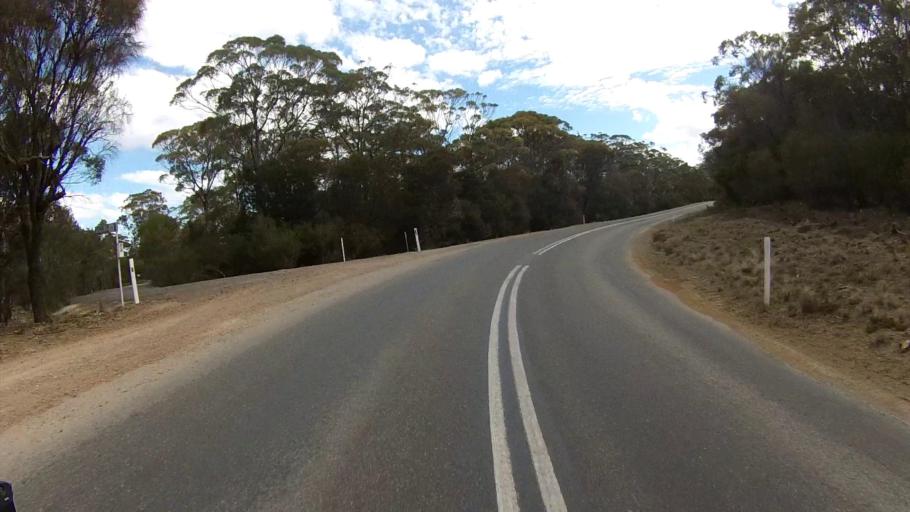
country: AU
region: Tasmania
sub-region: Break O'Day
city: St Helens
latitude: -41.9790
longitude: 148.1434
